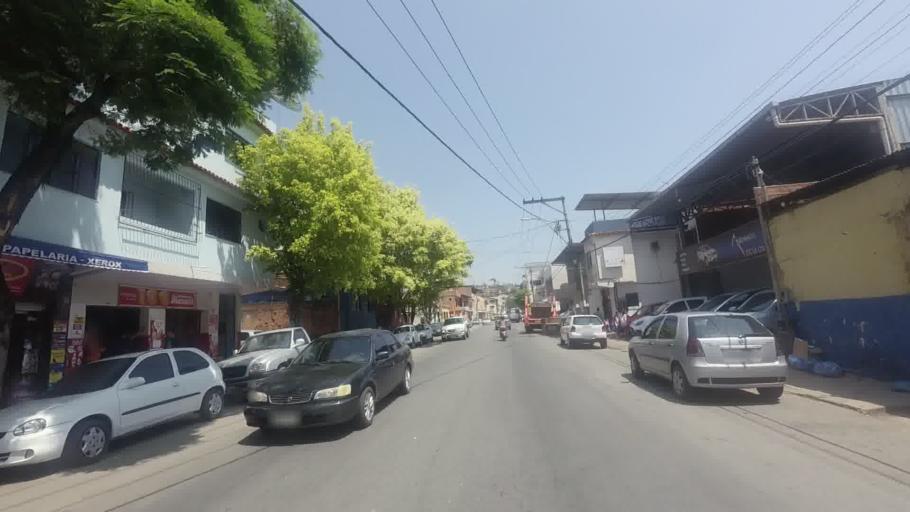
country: BR
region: Espirito Santo
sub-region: Cachoeiro De Itapemirim
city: Cachoeiro de Itapemirim
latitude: -20.8413
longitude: -41.1267
